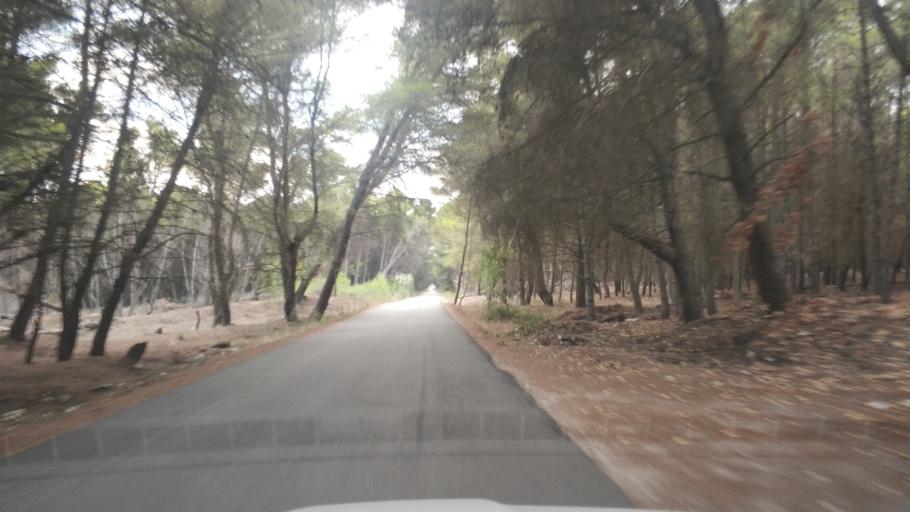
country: AL
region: Vlore
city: Vlore
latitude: 40.4955
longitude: 19.4333
